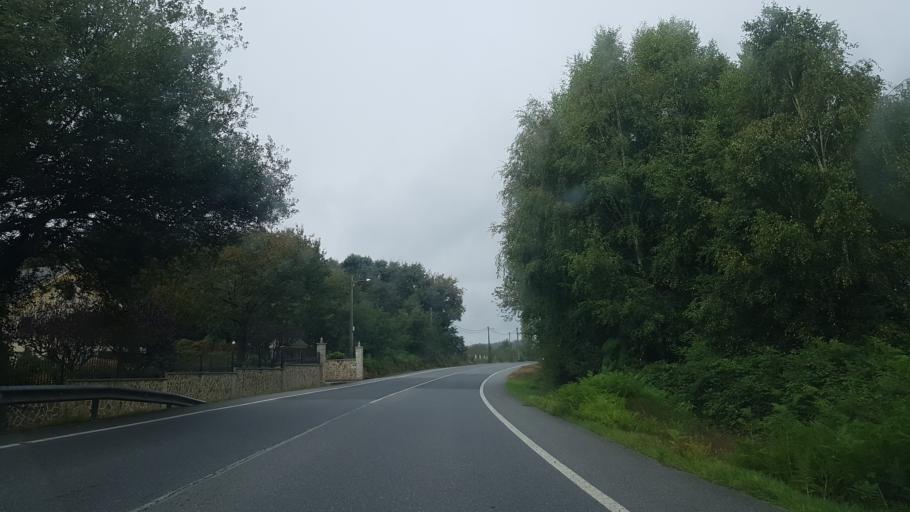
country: ES
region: Galicia
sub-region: Provincia de Lugo
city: Lugo
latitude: 42.9926
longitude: -7.6001
